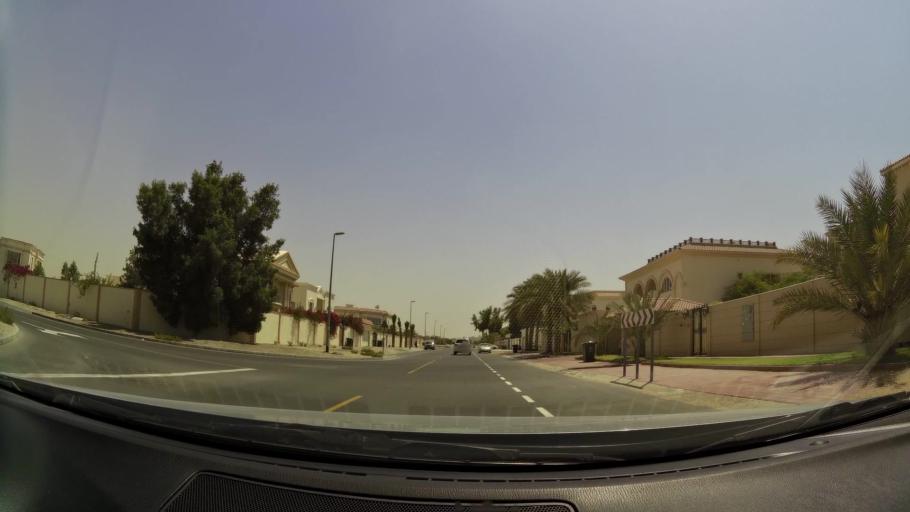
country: AE
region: Dubai
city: Dubai
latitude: 25.0973
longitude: 55.2151
